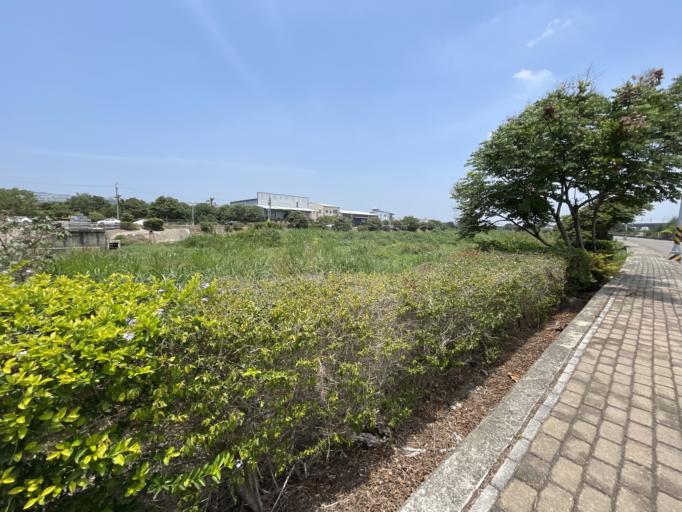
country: TW
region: Taiwan
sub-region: Taichung City
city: Taichung
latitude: 24.1929
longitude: 120.6299
